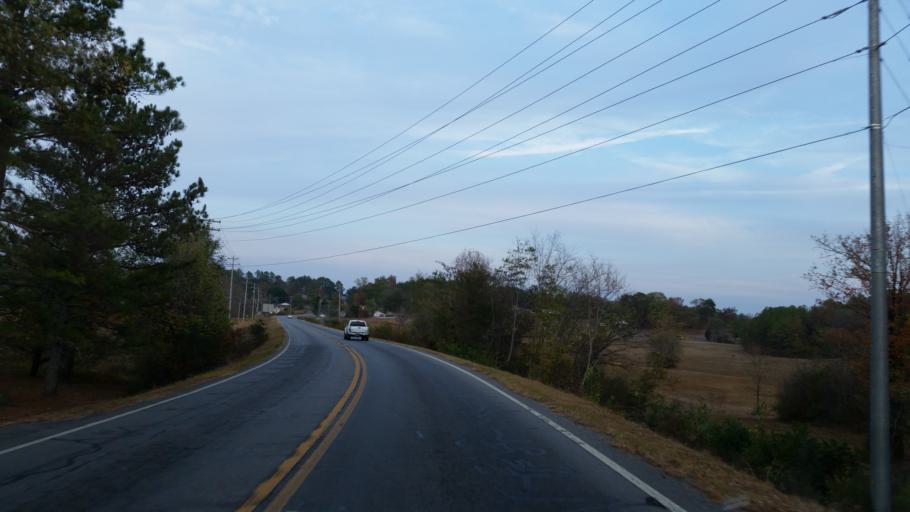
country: US
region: Georgia
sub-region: Gordon County
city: Calhoun
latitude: 34.5810
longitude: -84.9423
